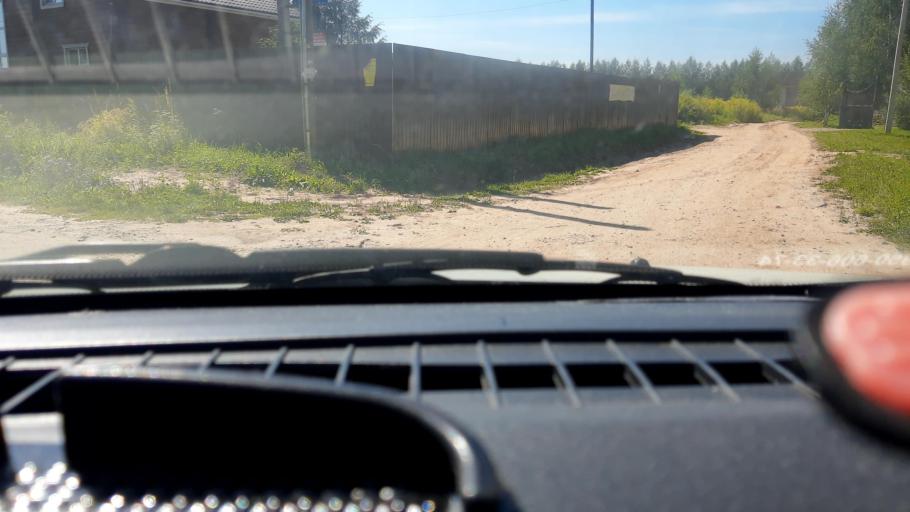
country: RU
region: Nizjnij Novgorod
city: Zavolzh'ye
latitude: 56.6923
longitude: 43.4180
